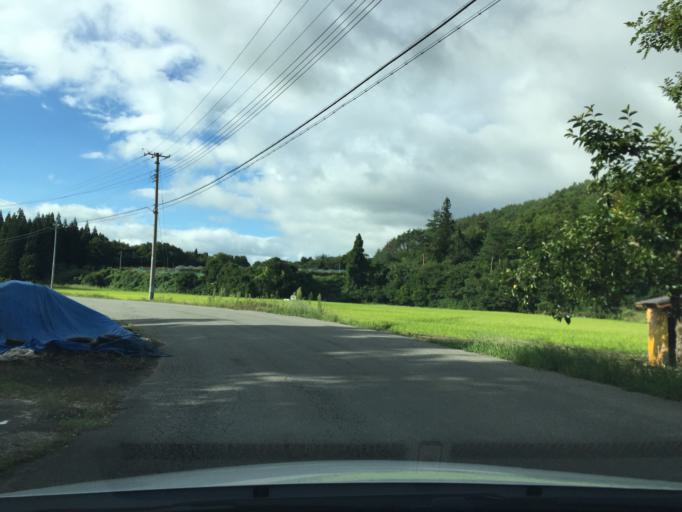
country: JP
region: Yamagata
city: Takahata
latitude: 37.9291
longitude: 140.2075
